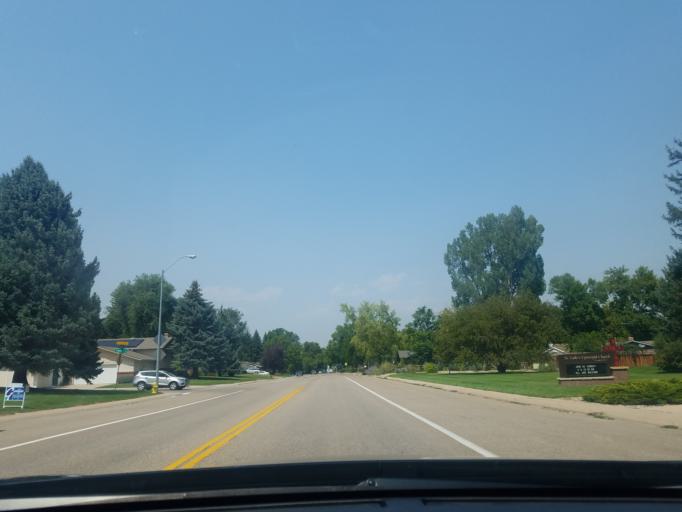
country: US
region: Colorado
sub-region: Larimer County
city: Fort Collins
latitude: 40.5609
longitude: -105.0667
